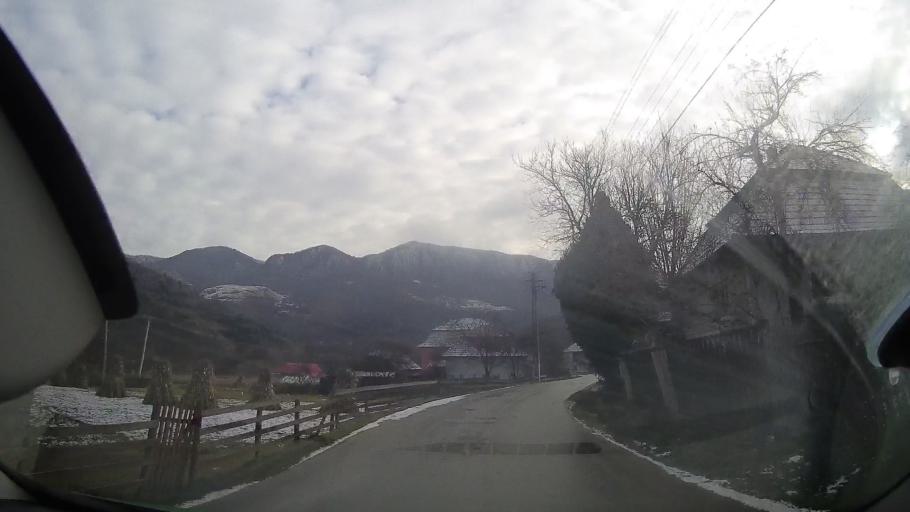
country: RO
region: Alba
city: Salciua de Sus
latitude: 46.4286
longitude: 23.4429
